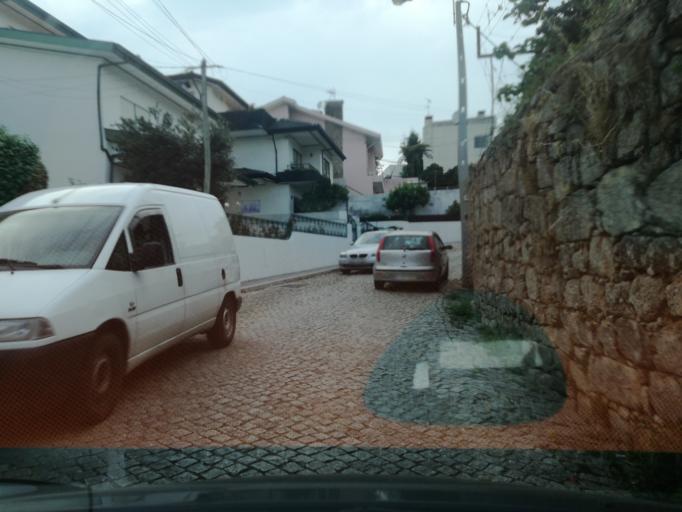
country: PT
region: Porto
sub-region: Maia
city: Maia
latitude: 41.2445
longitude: -8.6047
